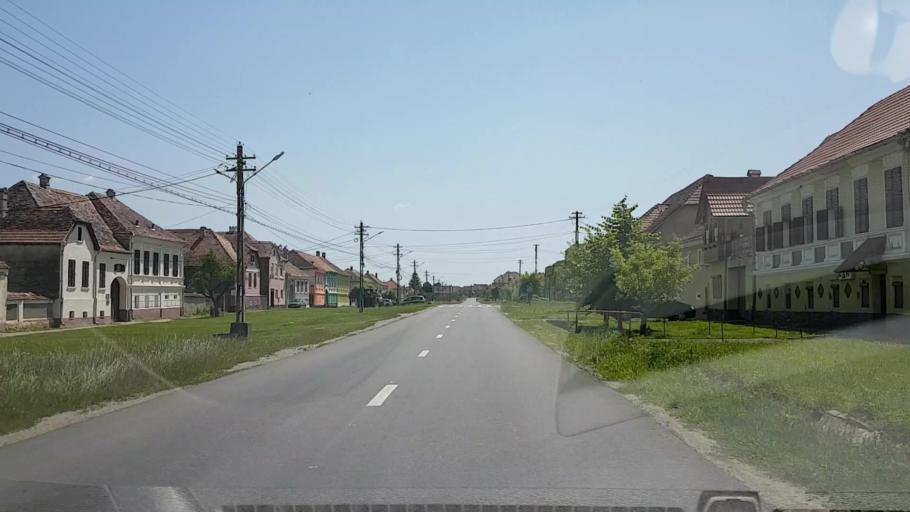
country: RO
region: Sibiu
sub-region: Comuna Merghindeal
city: Merghindeal
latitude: 45.9656
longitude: 24.7264
